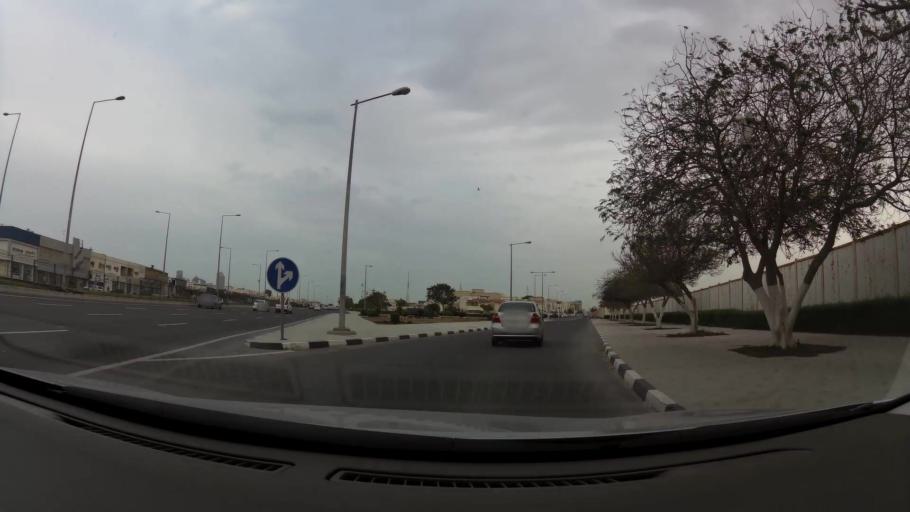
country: QA
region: Baladiyat ad Dawhah
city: Doha
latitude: 25.3207
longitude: 51.4894
